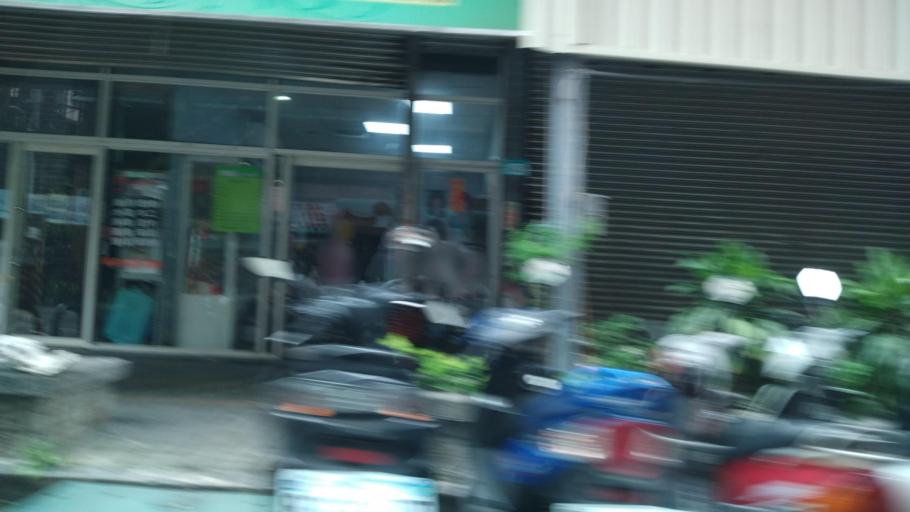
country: TW
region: Taipei
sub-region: Taipei
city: Banqiao
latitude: 24.9649
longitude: 121.4207
